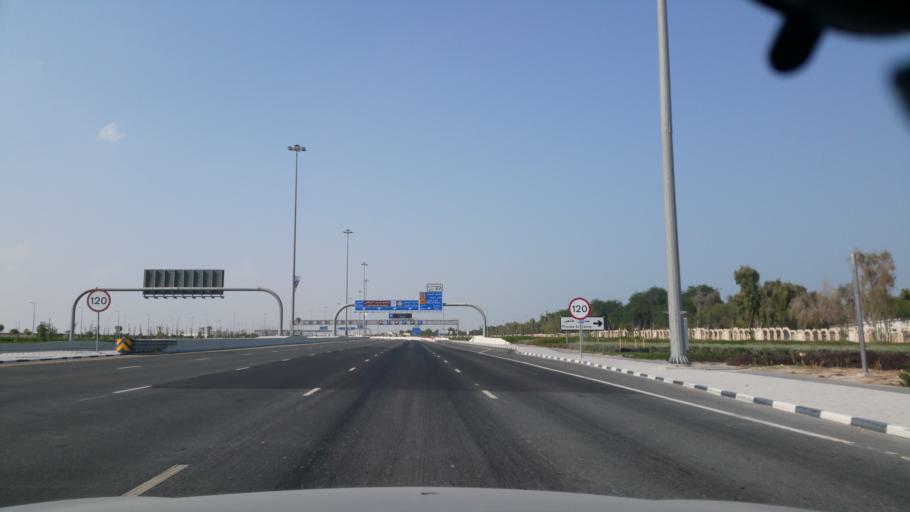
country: QA
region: Baladiyat Umm Salal
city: Umm Salal Muhammad
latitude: 25.3811
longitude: 51.5003
